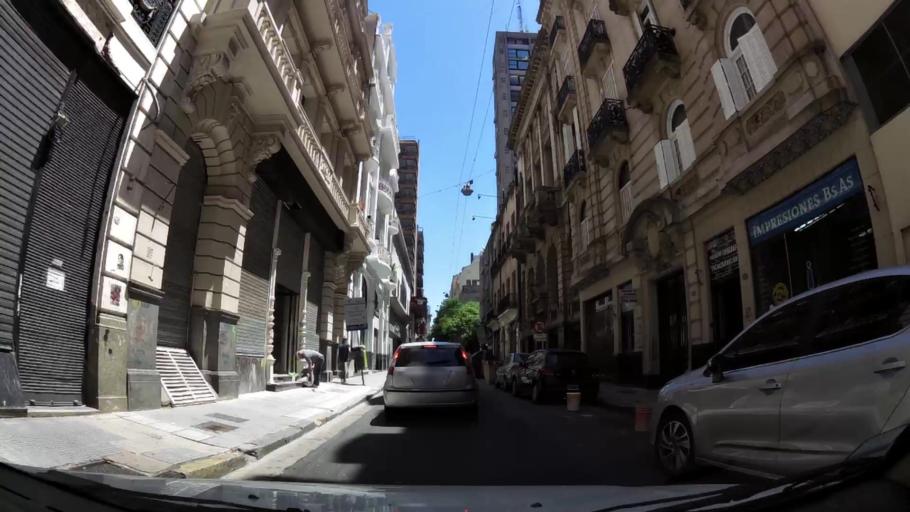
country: AR
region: Buenos Aires F.D.
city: Buenos Aires
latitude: -34.6081
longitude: -58.3771
